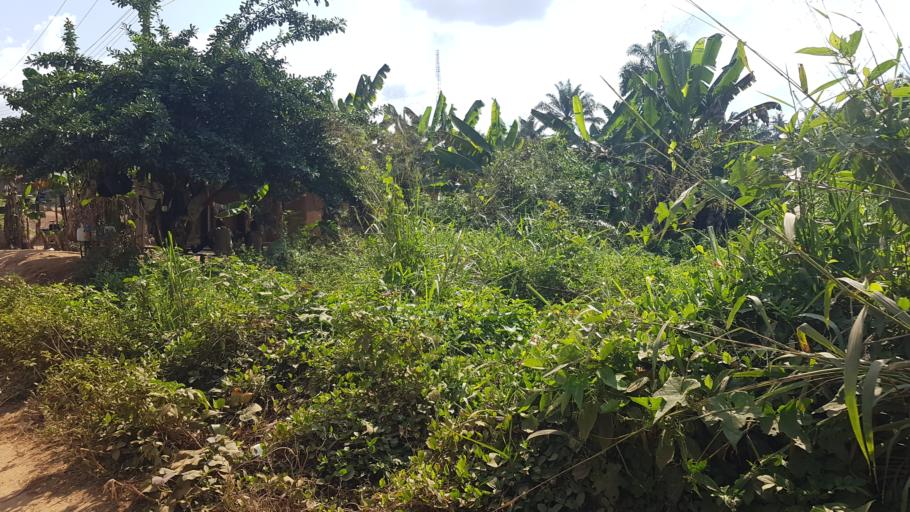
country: NG
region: Osun
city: Ifetedo
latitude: 7.0232
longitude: 4.6306
